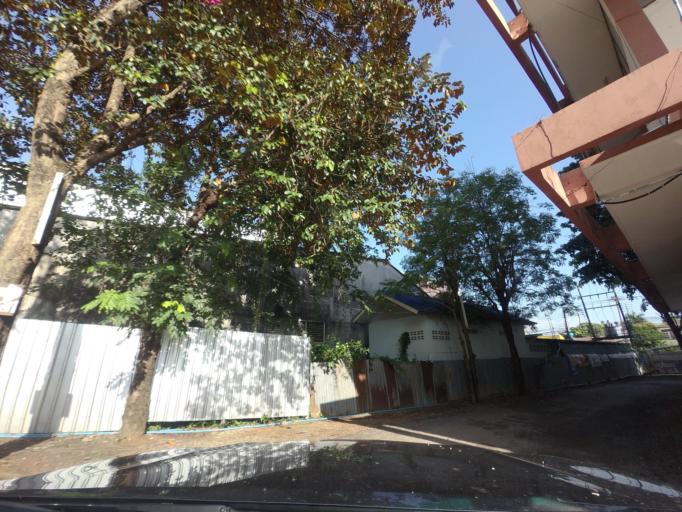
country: TH
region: Nong Khai
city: Nong Khai
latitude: 17.8832
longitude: 102.7486
